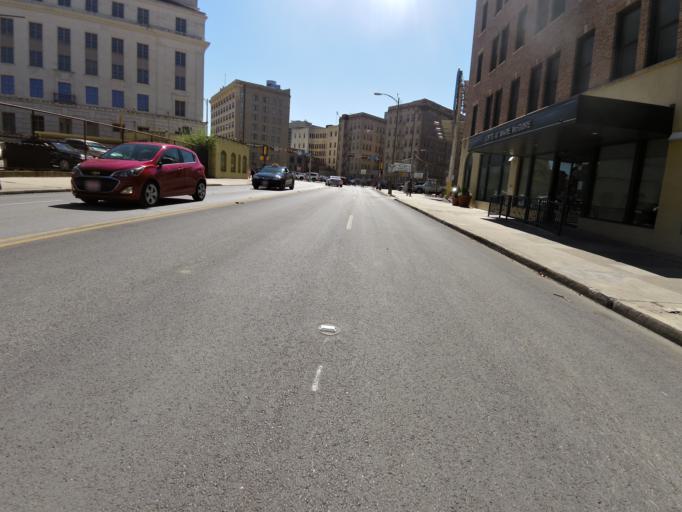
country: US
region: Texas
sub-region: Bexar County
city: San Antonio
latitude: 29.4281
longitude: -98.4863
